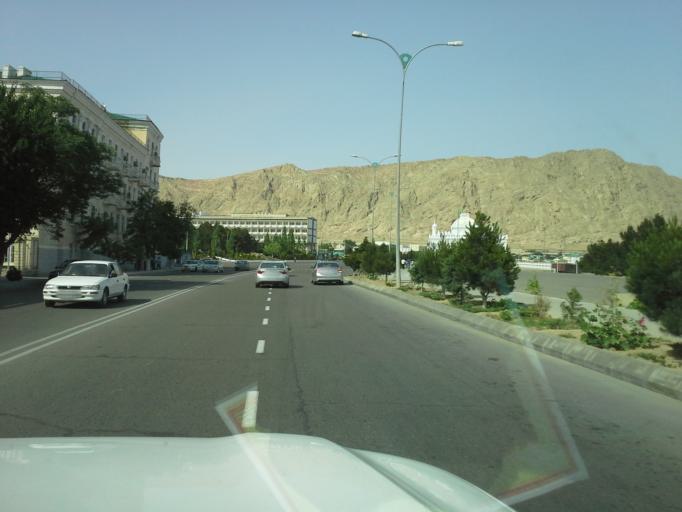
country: TM
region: Balkan
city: Turkmenbasy
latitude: 40.0027
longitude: 52.9934
